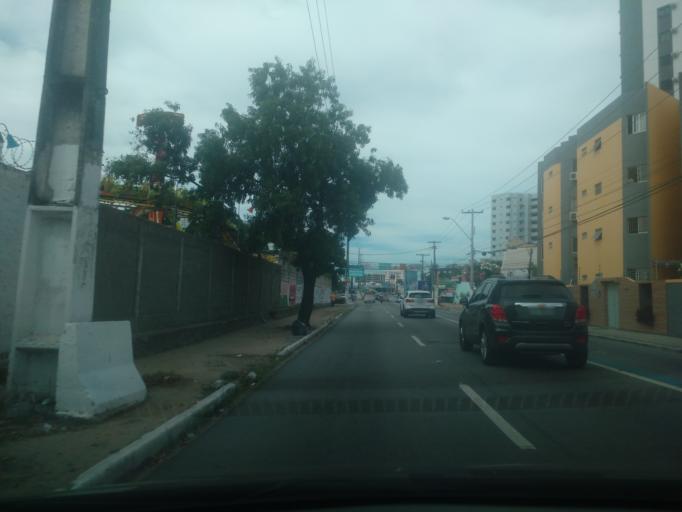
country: BR
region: Alagoas
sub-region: Maceio
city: Maceio
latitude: -9.6474
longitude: -35.7127
